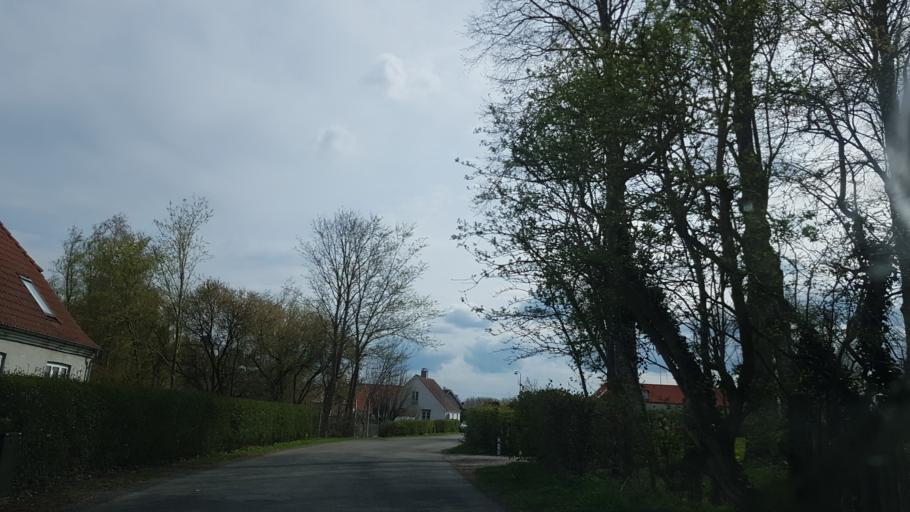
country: DK
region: Capital Region
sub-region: Allerod Kommune
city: Lillerod
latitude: 55.8958
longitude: 12.3276
